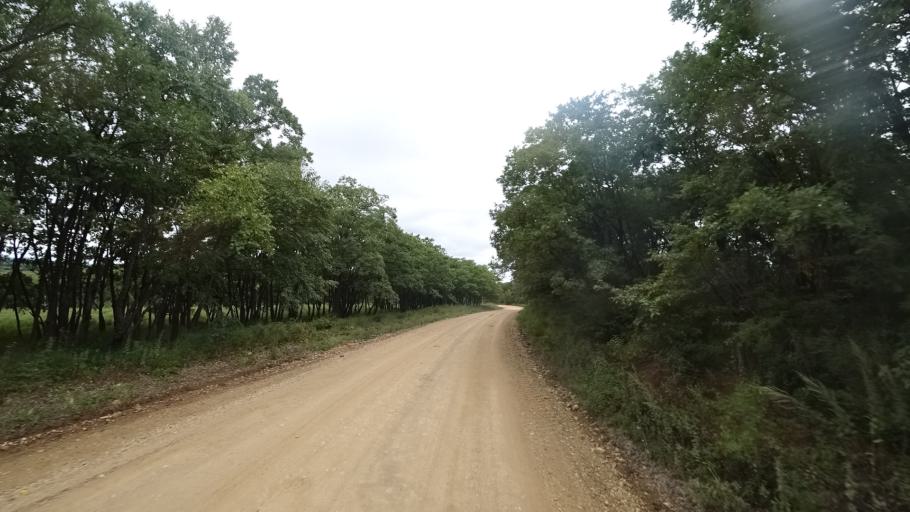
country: RU
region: Primorskiy
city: Chernigovka
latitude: 44.3400
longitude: 132.6214
